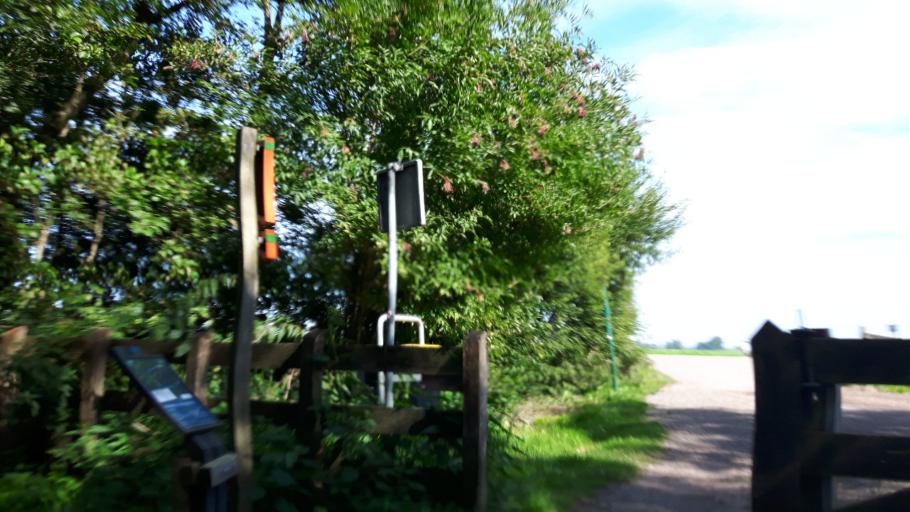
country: NL
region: Friesland
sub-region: Gemeente Skarsterlan
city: Joure
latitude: 52.9883
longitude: 5.7704
